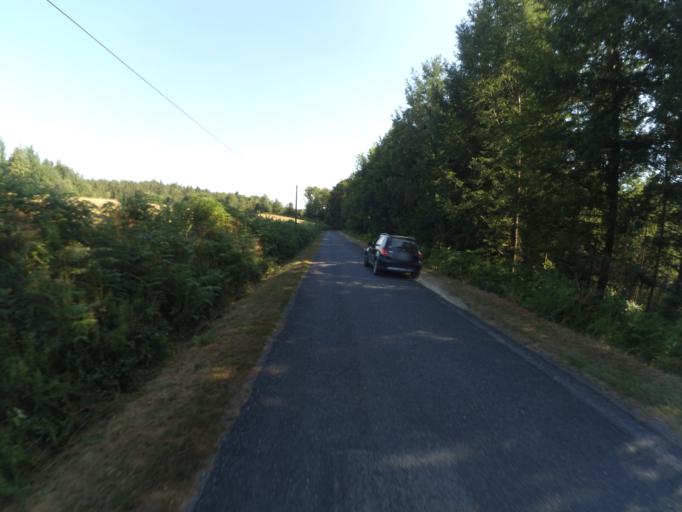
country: FR
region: Limousin
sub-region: Departement de la Haute-Vienne
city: Eymoutiers
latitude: 45.7397
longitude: 1.8190
